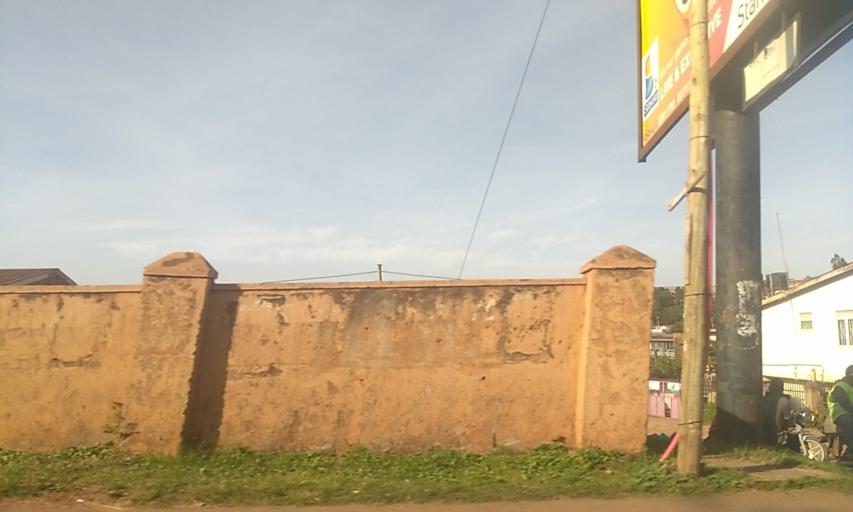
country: UG
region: Central Region
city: Kampala Central Division
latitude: 0.3433
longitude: 32.5930
